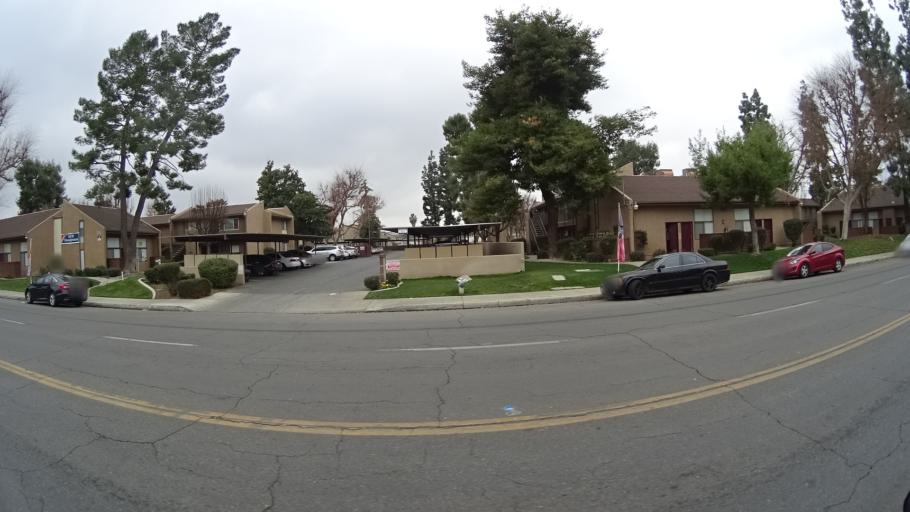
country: US
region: California
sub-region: Kern County
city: Bakersfield
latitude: 35.3932
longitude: -119.0105
